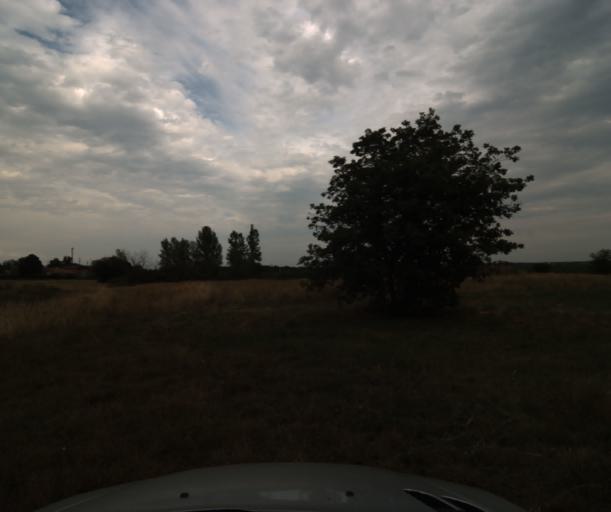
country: FR
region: Midi-Pyrenees
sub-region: Departement de la Haute-Garonne
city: Lherm
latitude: 43.4591
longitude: 1.1948
